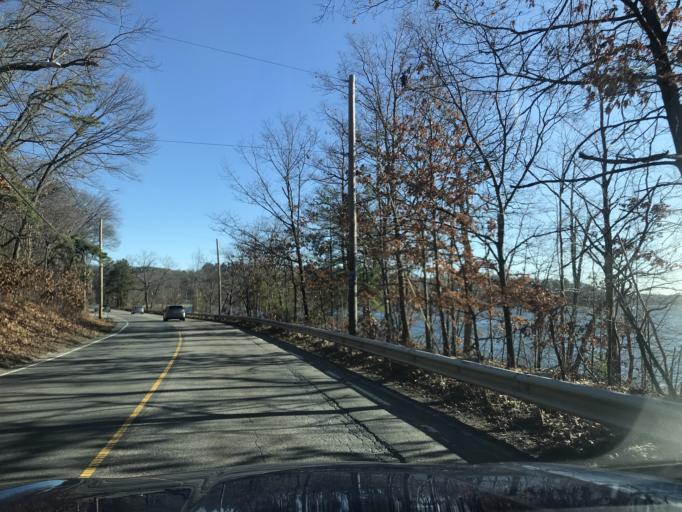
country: US
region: Massachusetts
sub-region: Essex County
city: North Andover
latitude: 42.7141
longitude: -71.1043
